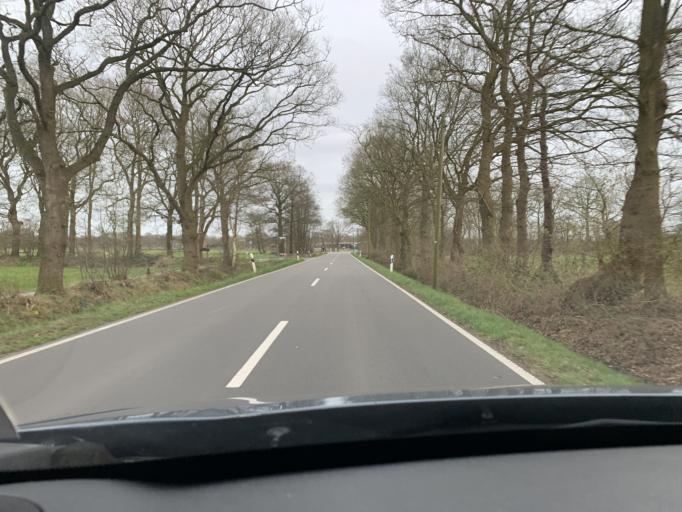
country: DE
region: Lower Saxony
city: Detern
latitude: 53.2599
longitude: 7.7096
